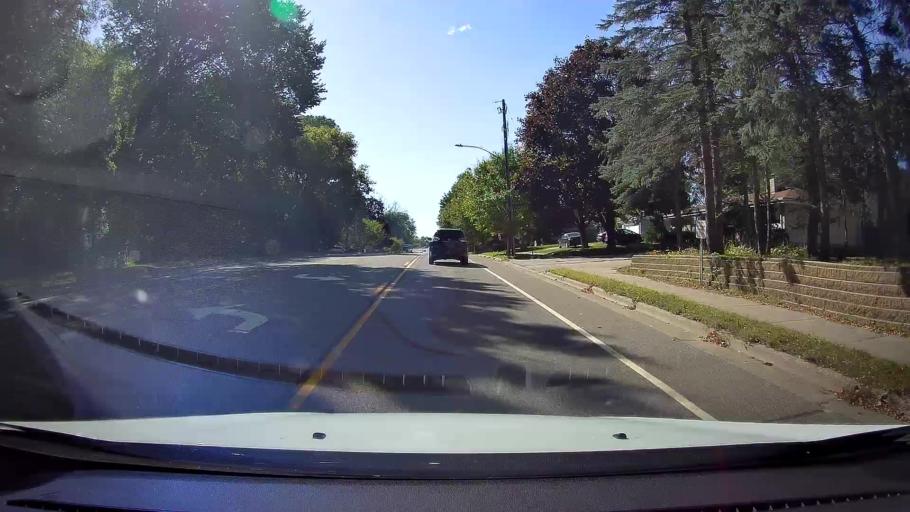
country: US
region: Minnesota
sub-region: Ramsey County
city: Roseville
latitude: 45.0156
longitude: -93.1568
